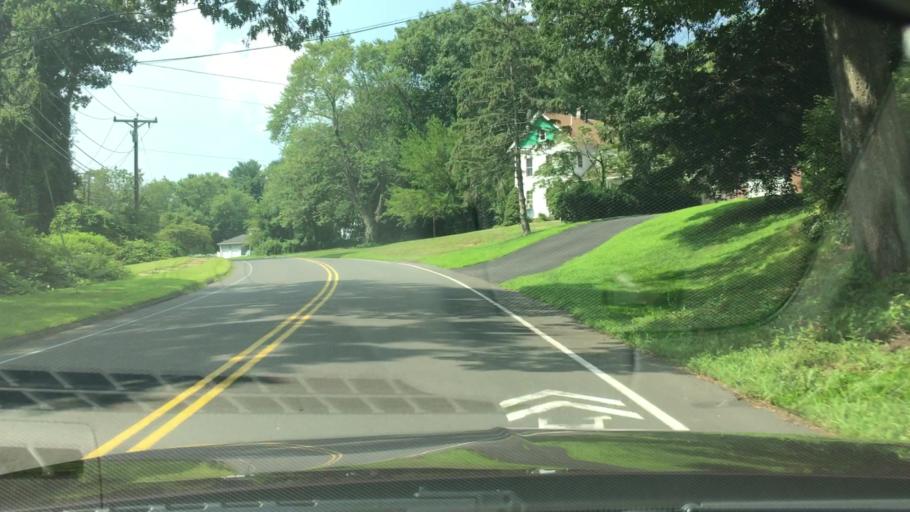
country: US
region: Connecticut
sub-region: Hartford County
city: Plainville
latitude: 41.6636
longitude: -72.8851
